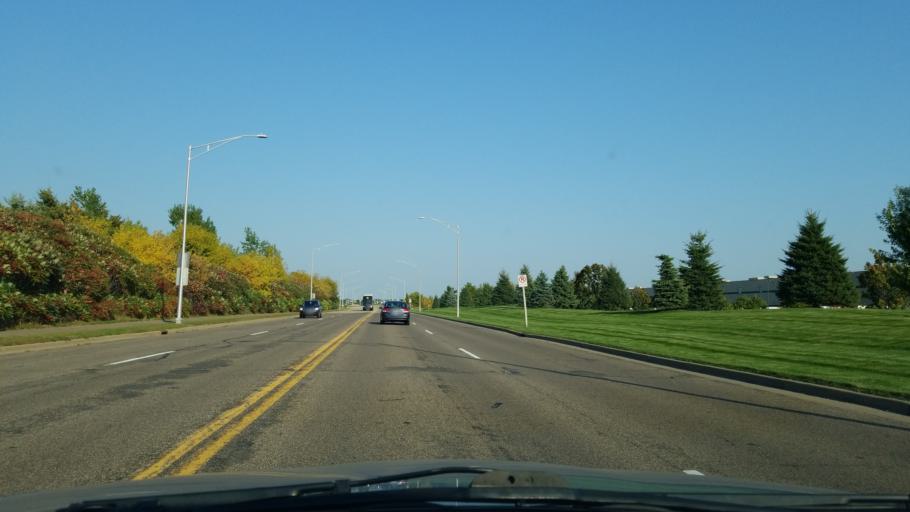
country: US
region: Wisconsin
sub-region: Saint Croix County
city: Hudson
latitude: 44.9489
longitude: -92.7038
